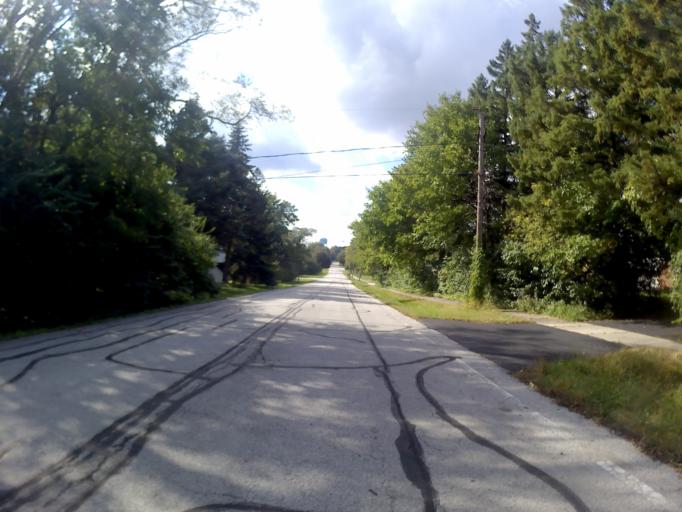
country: US
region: Illinois
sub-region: DuPage County
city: Lisle
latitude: 41.8045
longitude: -88.0883
